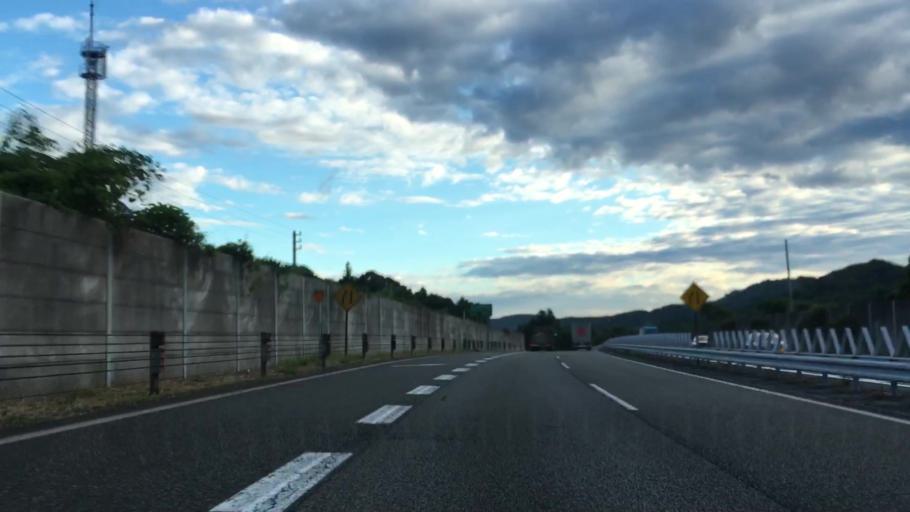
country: JP
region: Yamaguchi
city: Onoda
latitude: 34.1460
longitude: 131.2329
